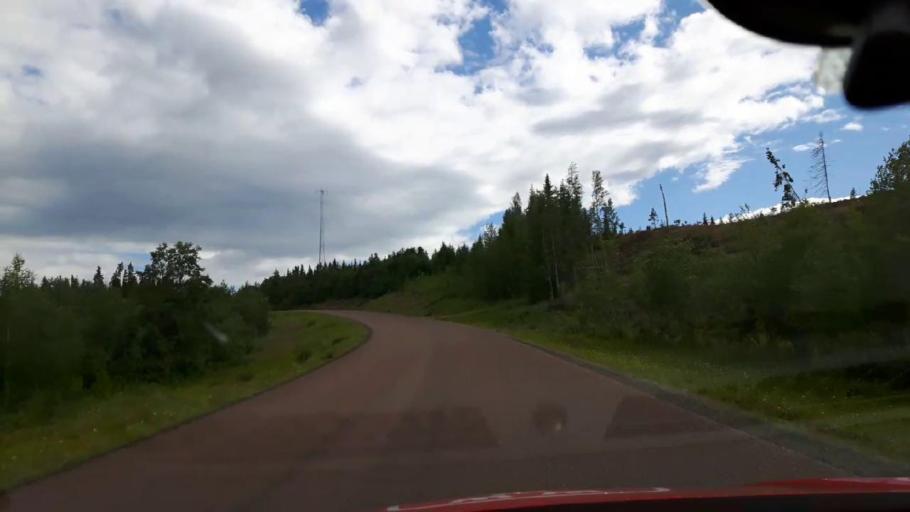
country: SE
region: Jaemtland
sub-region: Are Kommun
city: Are
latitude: 63.3008
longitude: 13.2225
